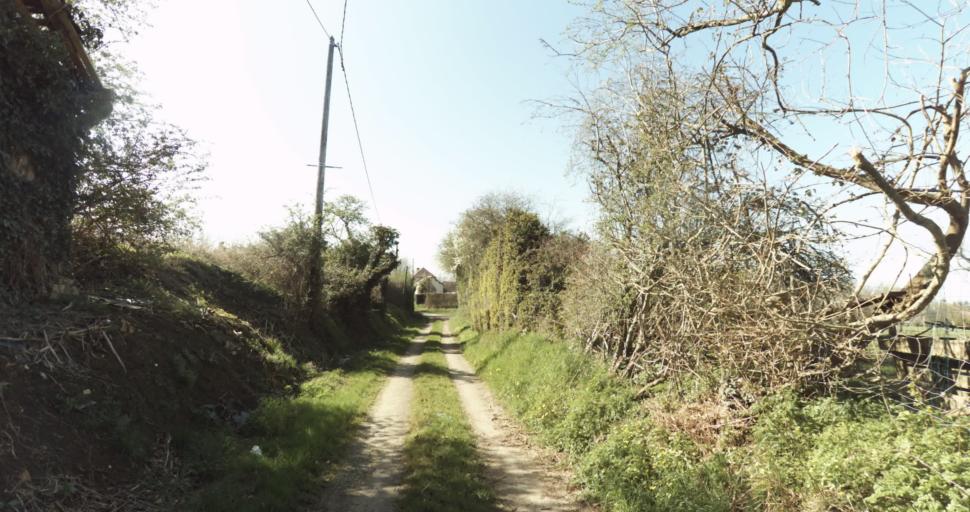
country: FR
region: Lower Normandy
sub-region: Departement du Calvados
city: Saint-Pierre-sur-Dives
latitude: 48.9410
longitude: -0.0026
